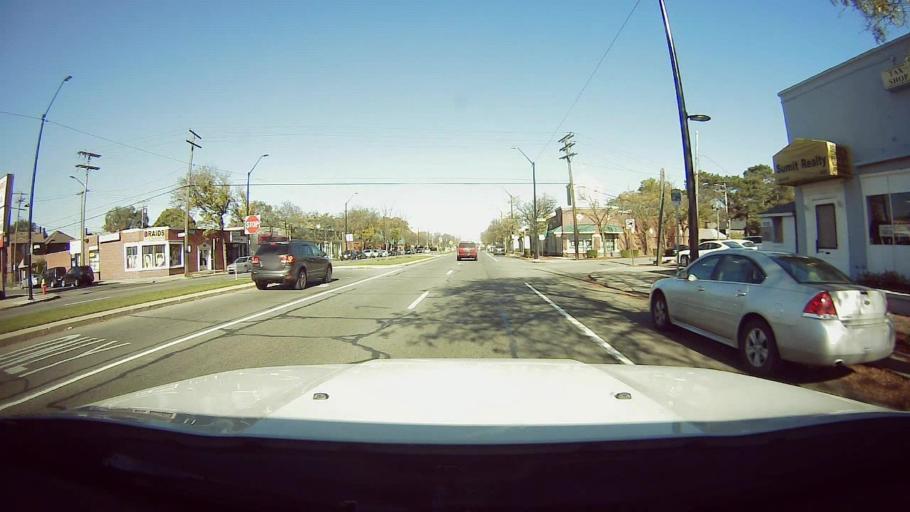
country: US
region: Michigan
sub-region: Oakland County
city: Ferndale
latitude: 42.4332
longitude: -83.1414
